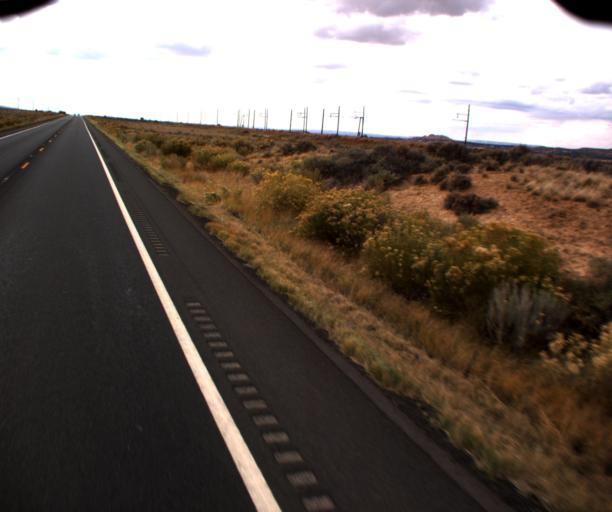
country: US
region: Arizona
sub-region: Navajo County
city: Kayenta
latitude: 36.5355
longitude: -110.5586
